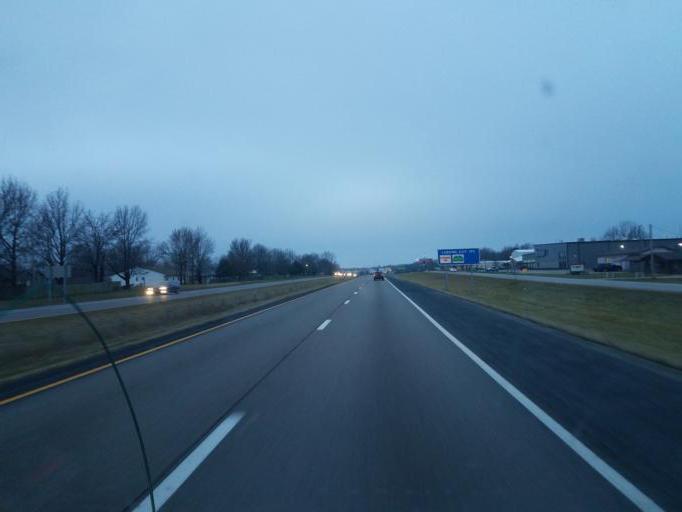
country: US
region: Missouri
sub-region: Phelps County
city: Saint James
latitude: 38.0097
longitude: -91.6064
